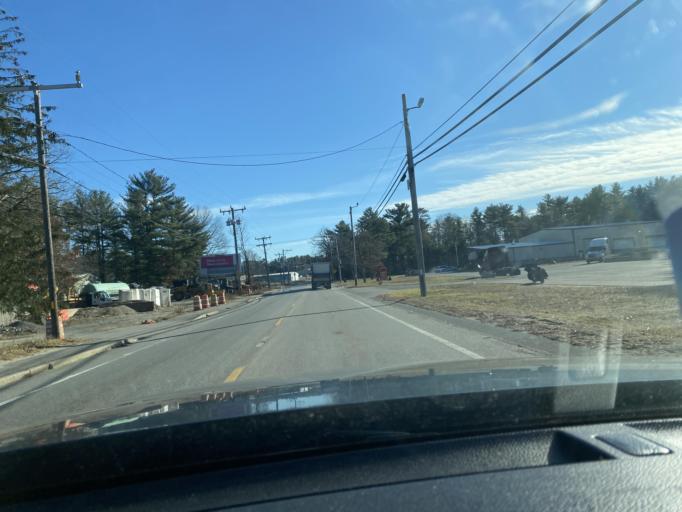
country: US
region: Massachusetts
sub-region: Plymouth County
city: West Wareham
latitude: 41.7848
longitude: -70.7468
